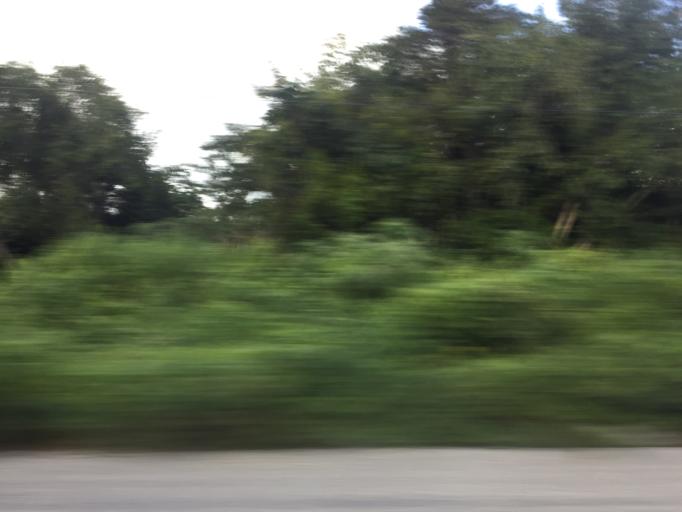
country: MX
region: Quintana Roo
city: Tulum
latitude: 20.2832
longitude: -87.4962
